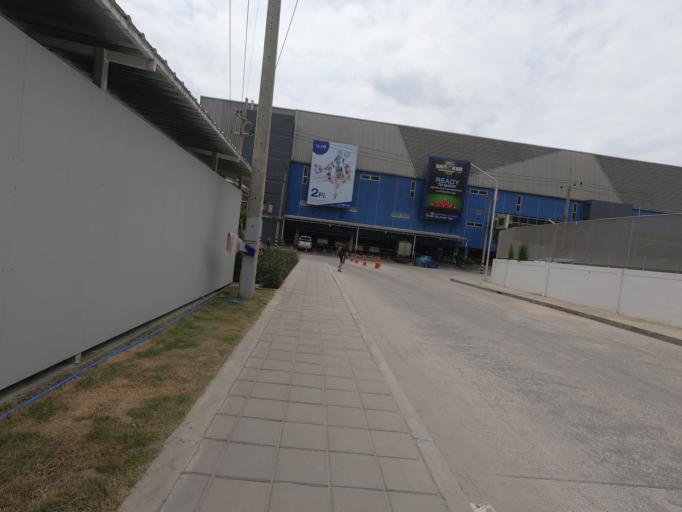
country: TH
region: Bangkok
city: Sai Mai
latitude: 13.9426
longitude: 100.6518
